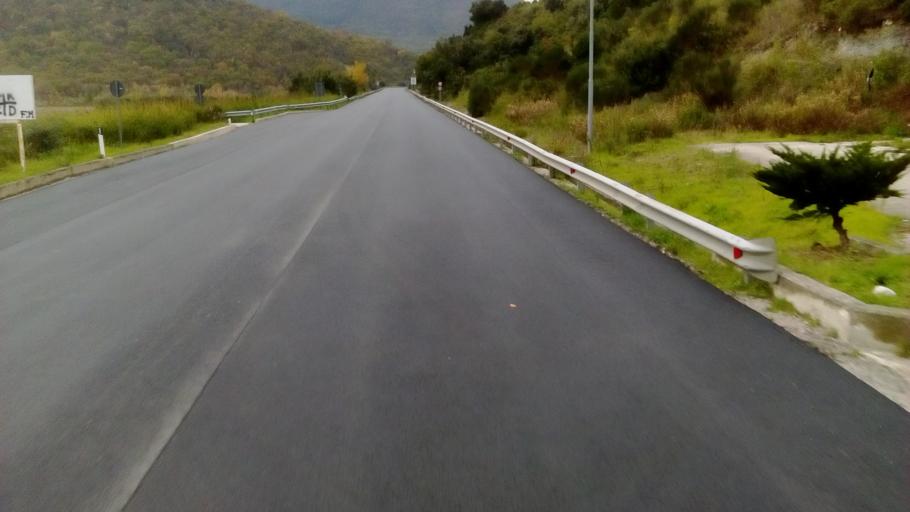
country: IT
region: Molise
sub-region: Provincia di Campobasso
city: Montemitro
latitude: 41.9181
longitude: 14.6615
